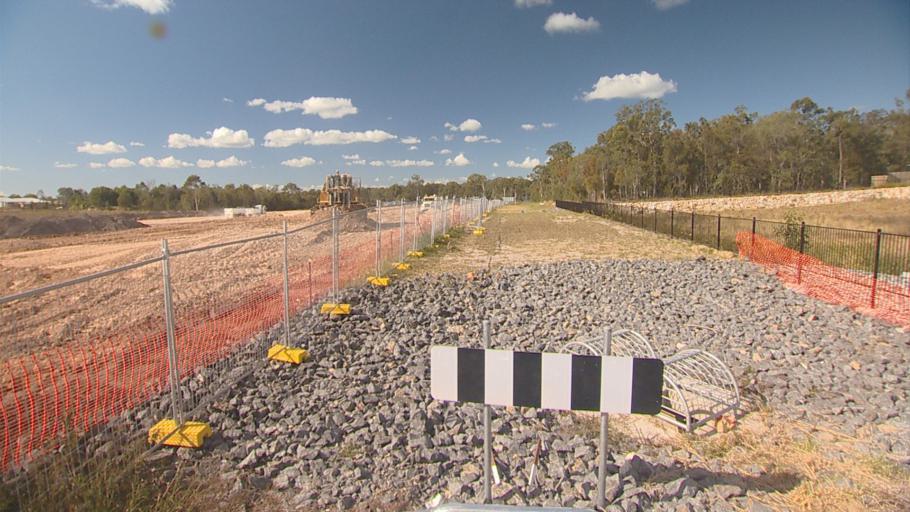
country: AU
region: Queensland
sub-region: Logan
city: Logan Reserve
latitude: -27.7150
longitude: 153.0888
